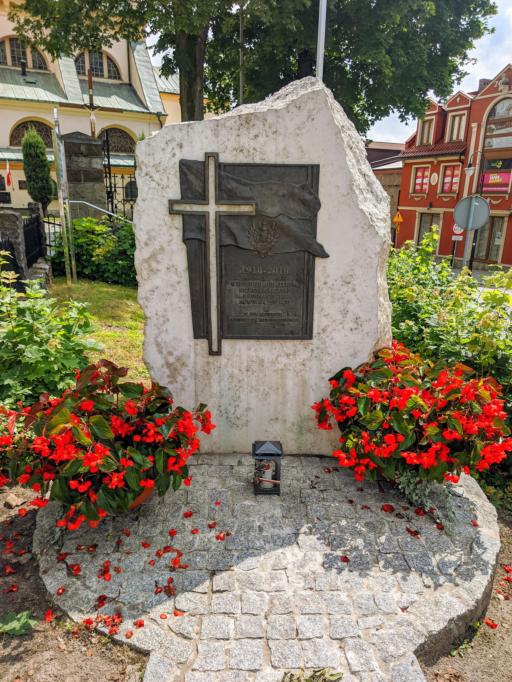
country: PL
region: Silesian Voivodeship
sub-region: Powiat klobucki
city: Klobuck
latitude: 50.9042
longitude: 18.9365
